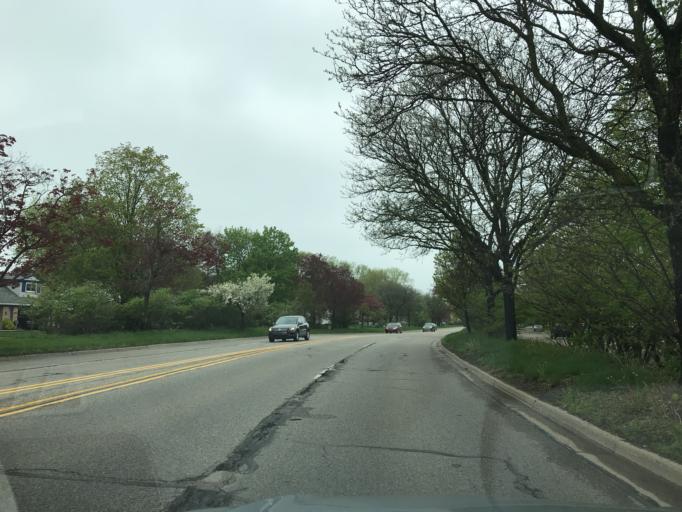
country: US
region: Michigan
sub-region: Washtenaw County
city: Ann Arbor
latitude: 42.2441
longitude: -83.7206
